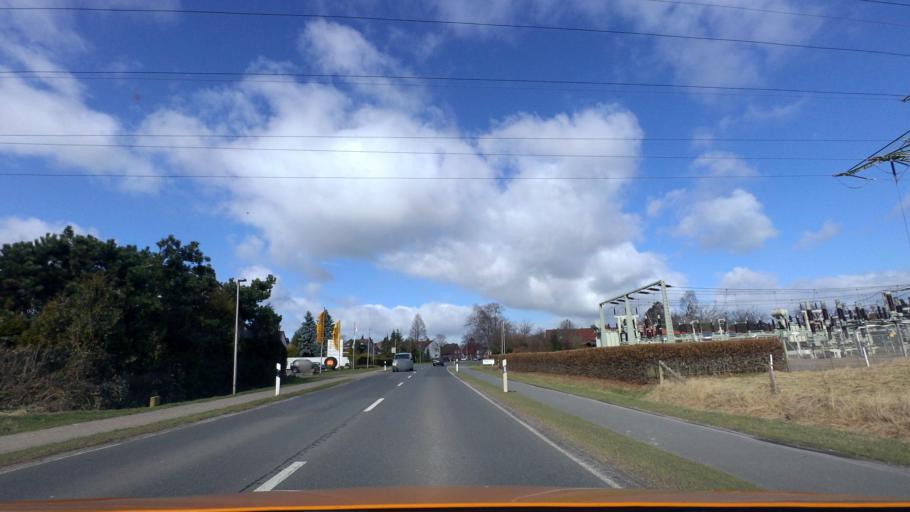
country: DE
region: Lower Saxony
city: Bad Zwischenahn
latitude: 53.1740
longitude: 7.9963
